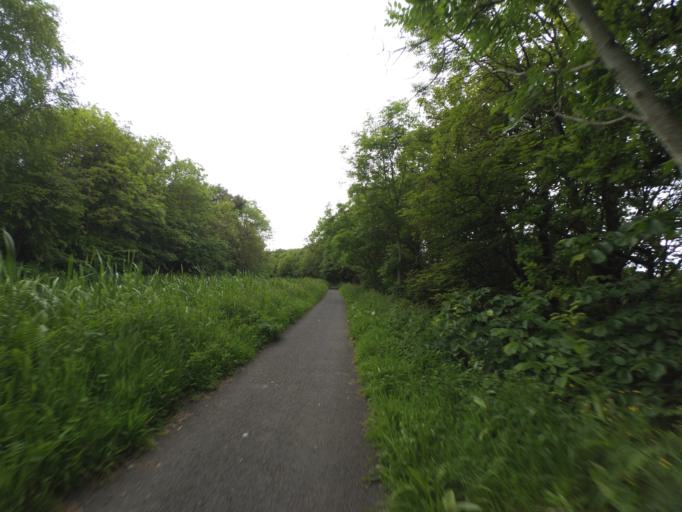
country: GB
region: Scotland
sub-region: West Lothian
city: Broxburn
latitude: 55.9680
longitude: -3.4674
